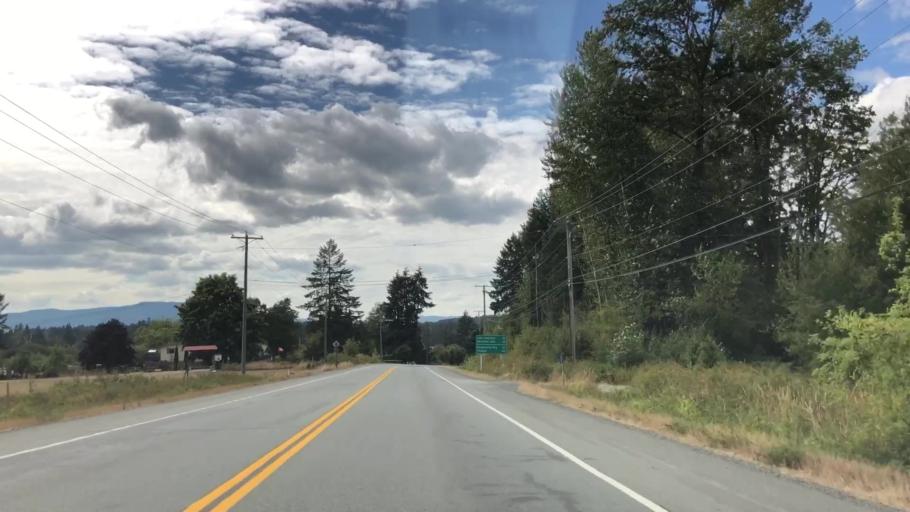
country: CA
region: British Columbia
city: Duncan
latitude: 48.8150
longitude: -123.7245
